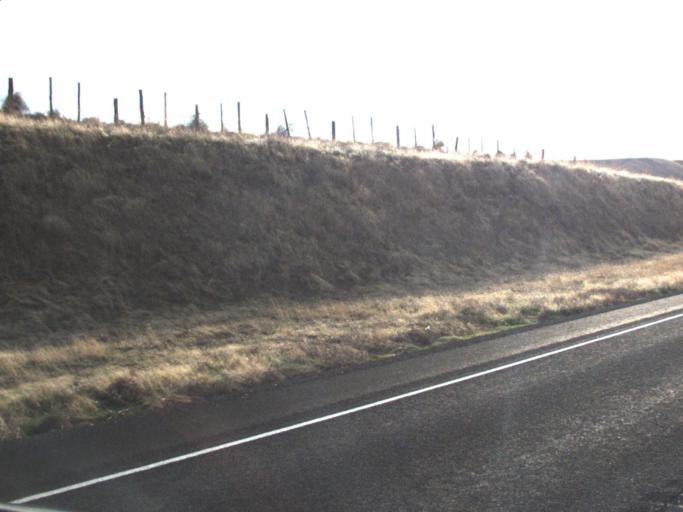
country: US
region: Washington
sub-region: Columbia County
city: Dayton
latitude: 46.5249
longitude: -117.9279
